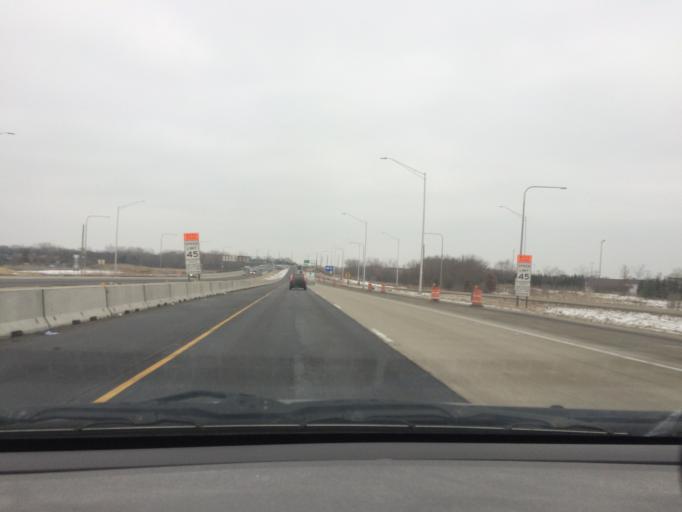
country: US
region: Illinois
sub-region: DuPage County
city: Roselle
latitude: 41.9974
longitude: -88.0984
